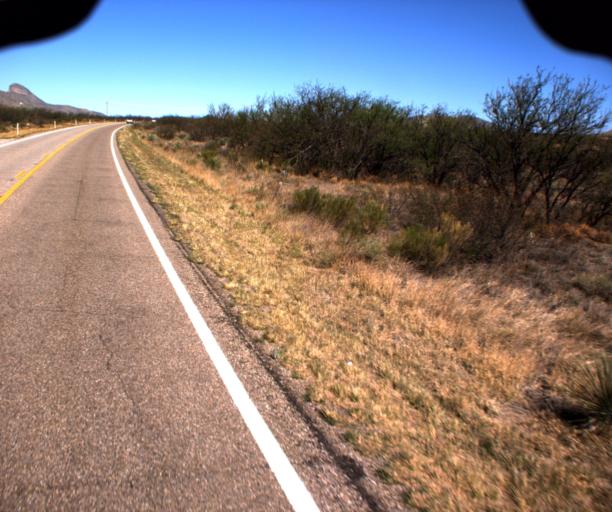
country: US
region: Arizona
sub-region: Cochise County
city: Huachuca City
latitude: 31.6953
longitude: -110.4182
